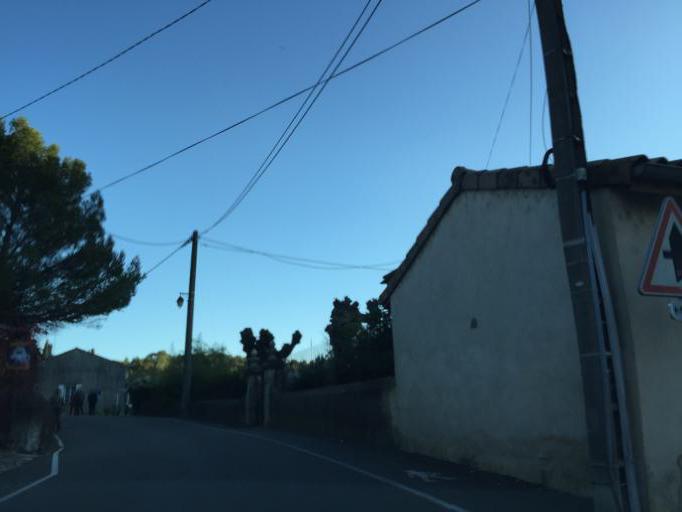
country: FR
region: Rhone-Alpes
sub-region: Departement de l'Ardeche
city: Bourg-Saint-Andeol
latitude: 44.4401
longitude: 4.6244
